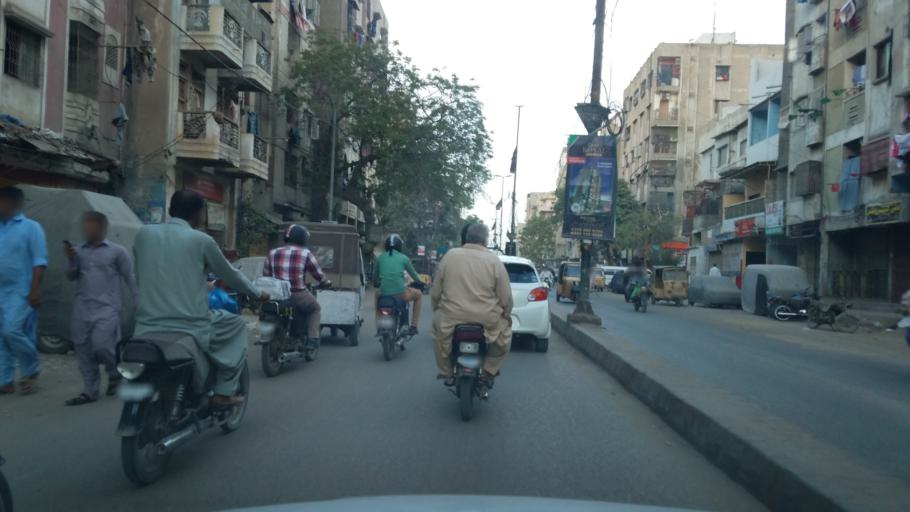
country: PK
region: Sindh
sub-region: Karachi District
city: Karachi
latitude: 24.8746
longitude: 67.0300
